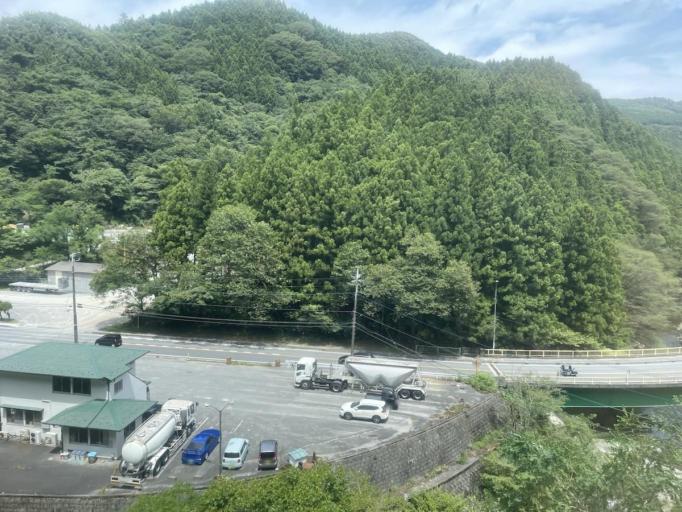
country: JP
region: Saitama
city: Chichibu
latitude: 35.9727
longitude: 139.1201
